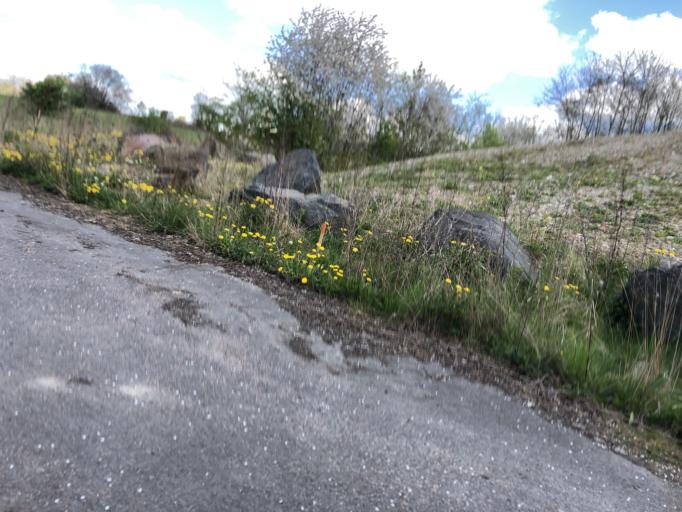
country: SE
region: Skane
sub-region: Lunds Kommun
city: Genarp
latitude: 55.6577
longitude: 13.3771
